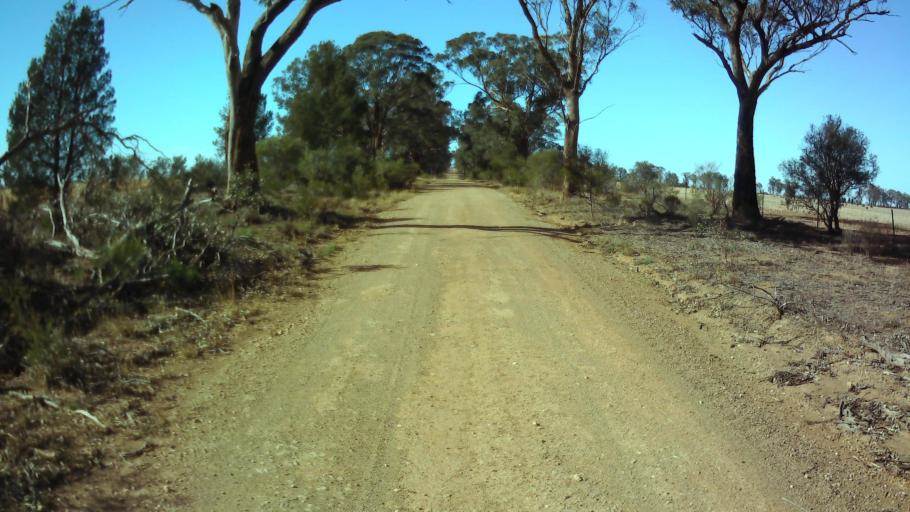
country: AU
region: New South Wales
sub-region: Weddin
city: Grenfell
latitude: -33.8945
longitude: 147.8798
